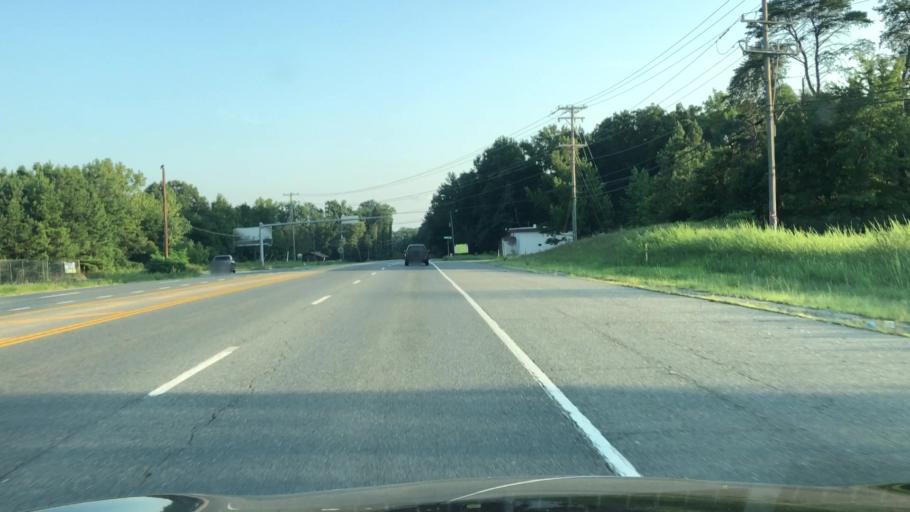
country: US
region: Virginia
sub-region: Stafford County
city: Falmouth
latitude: 38.3616
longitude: -77.4576
